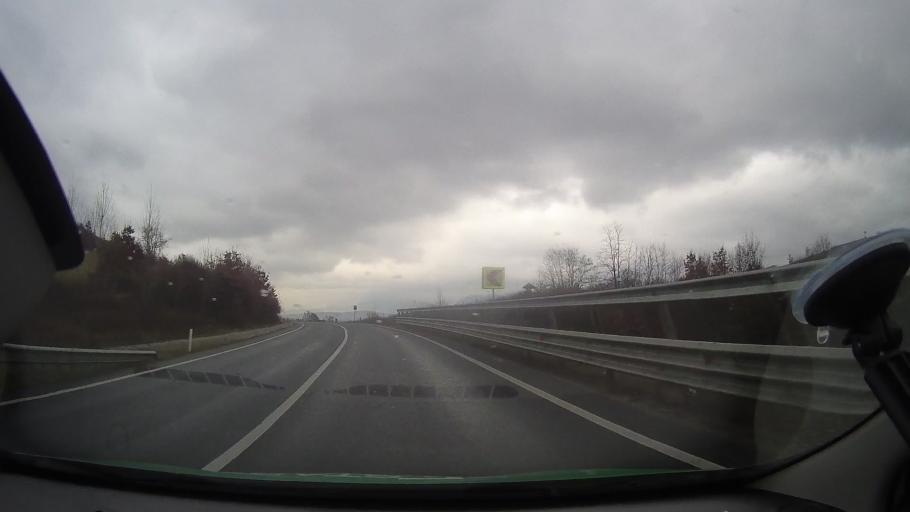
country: RO
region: Hunedoara
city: Vata de Jos
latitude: 46.2077
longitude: 22.5808
